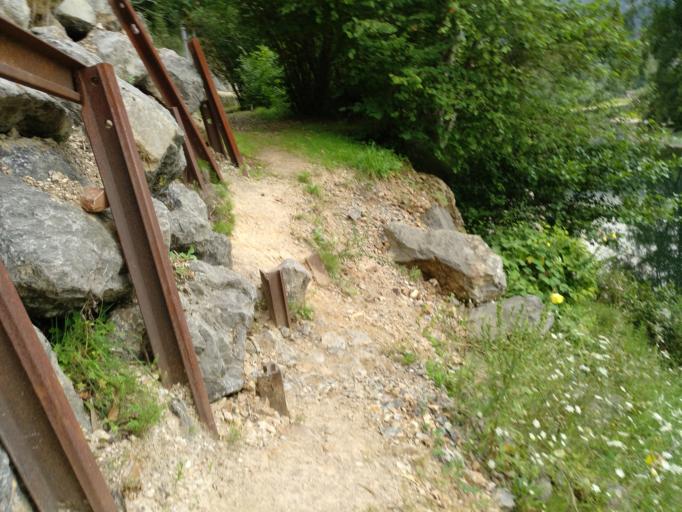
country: ES
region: Asturias
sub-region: Province of Asturias
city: Ribadesella
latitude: 43.4335
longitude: -5.0698
